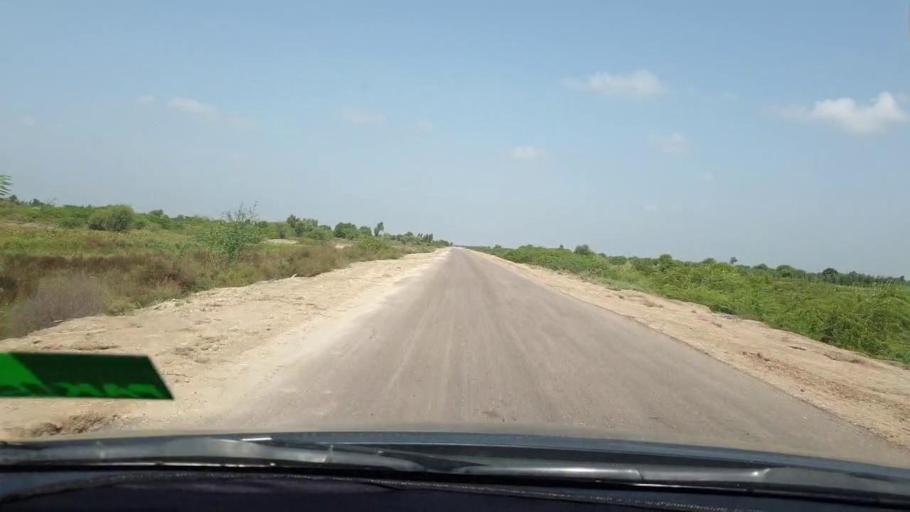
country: PK
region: Sindh
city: Digri
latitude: 24.9797
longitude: 69.1279
